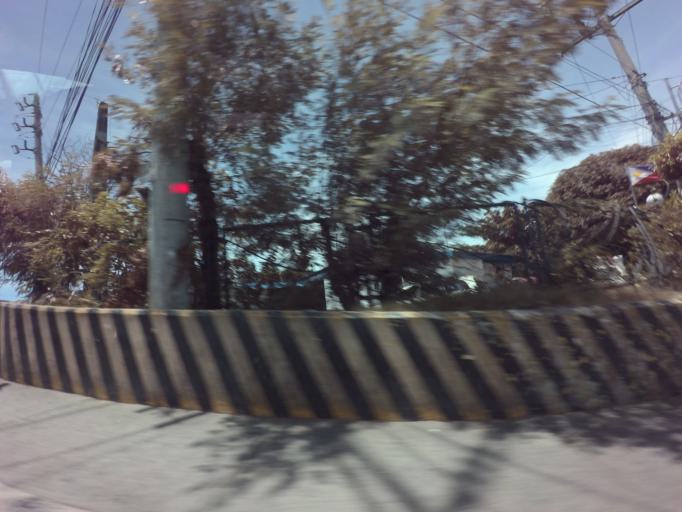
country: PH
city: Sambayanihan People's Village
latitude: 14.4921
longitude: 120.9922
